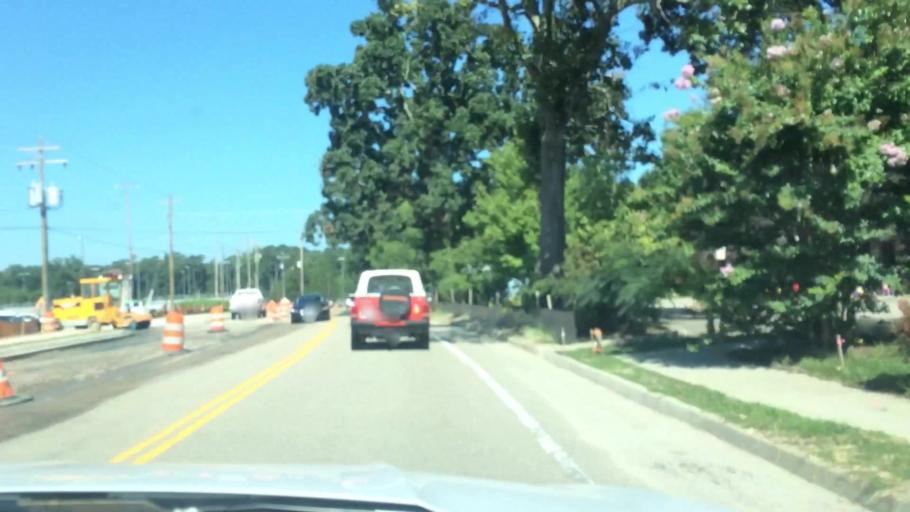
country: US
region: Virginia
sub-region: James City County
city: Williamsburg
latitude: 37.2921
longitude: -76.7255
